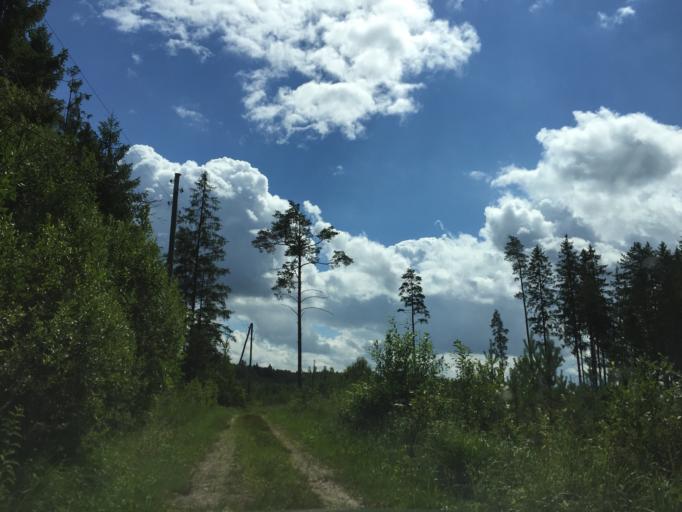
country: LV
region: Ropazu
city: Ropazi
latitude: 56.8971
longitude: 24.7164
